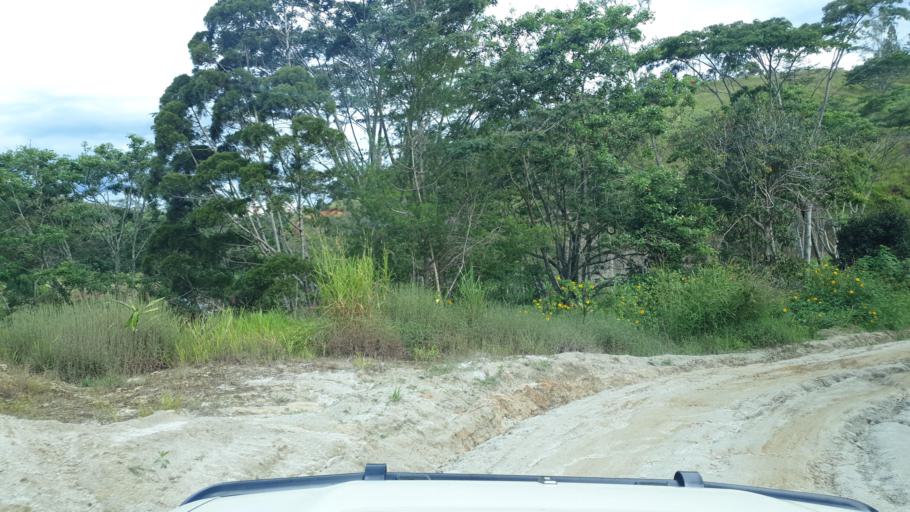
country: PG
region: Eastern Highlands
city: Goroka
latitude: -5.9251
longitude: 145.2628
